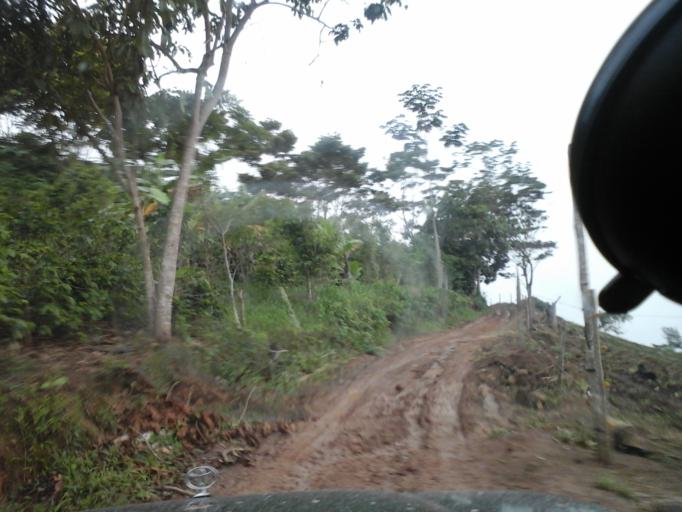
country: CO
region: Cesar
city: Agustin Codazzi
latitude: 9.9610
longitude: -73.0613
